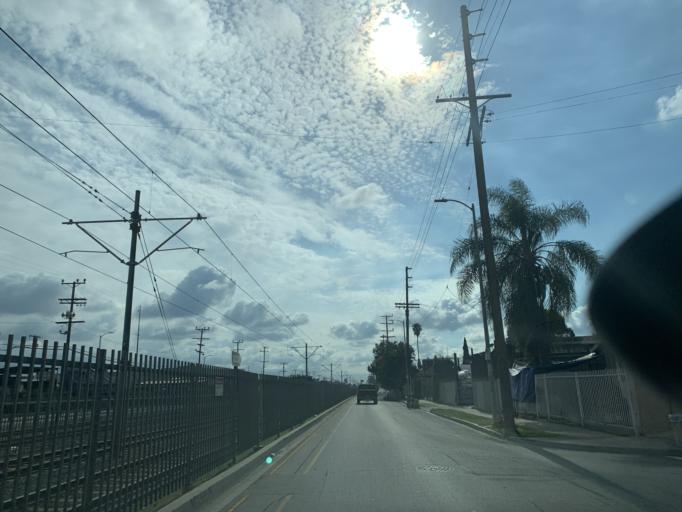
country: US
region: California
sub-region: Los Angeles County
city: Huntington Park
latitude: 34.0112
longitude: -118.2433
